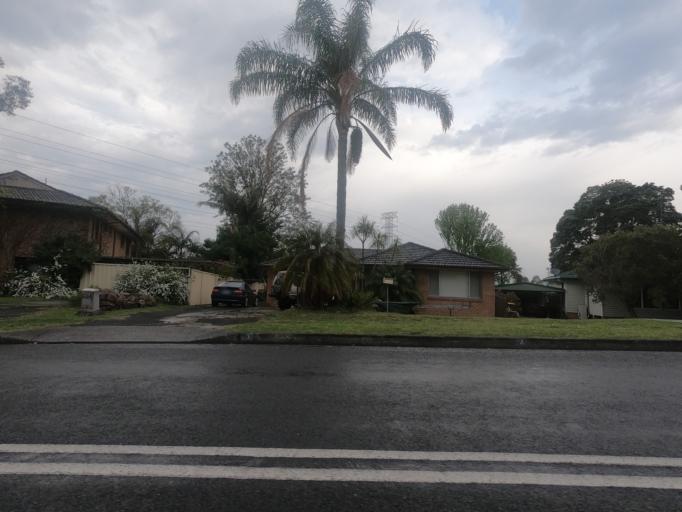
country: AU
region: New South Wales
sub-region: Wollongong
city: Koonawarra
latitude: -34.4950
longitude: 150.8086
